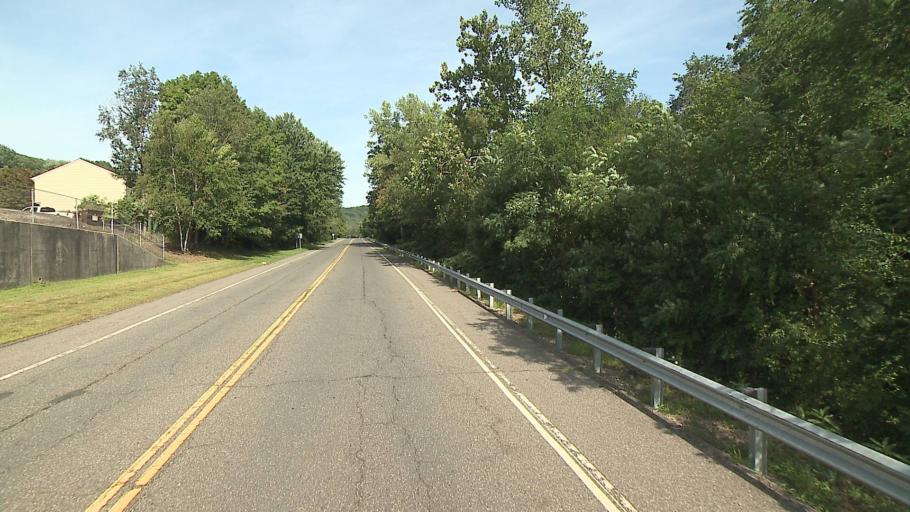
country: US
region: Connecticut
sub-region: Litchfield County
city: Thomaston
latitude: 41.6710
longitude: -73.0819
